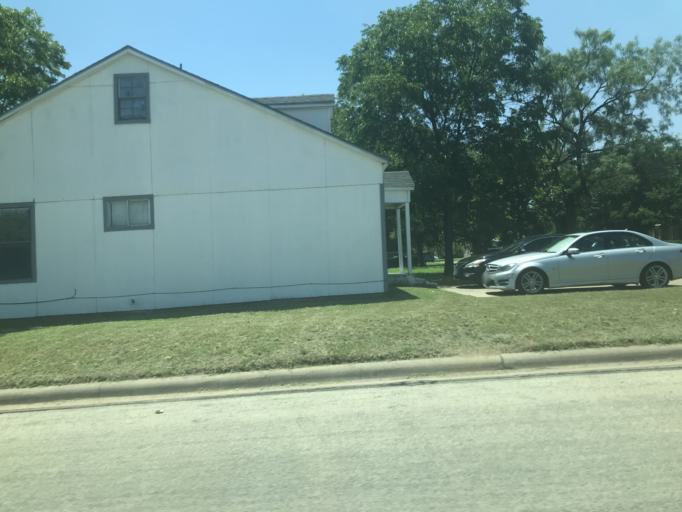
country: US
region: Texas
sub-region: Taylor County
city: Abilene
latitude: 32.4646
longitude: -99.7124
